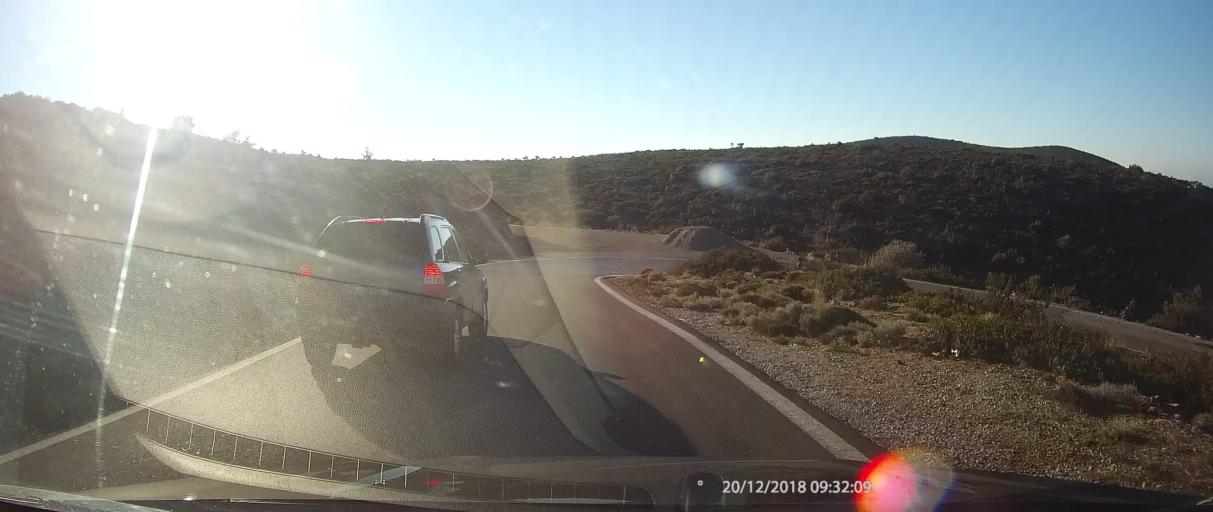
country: GR
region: Peloponnese
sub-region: Nomos Lakonias
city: Kato Glikovrisi
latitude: 36.9464
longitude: 22.8357
